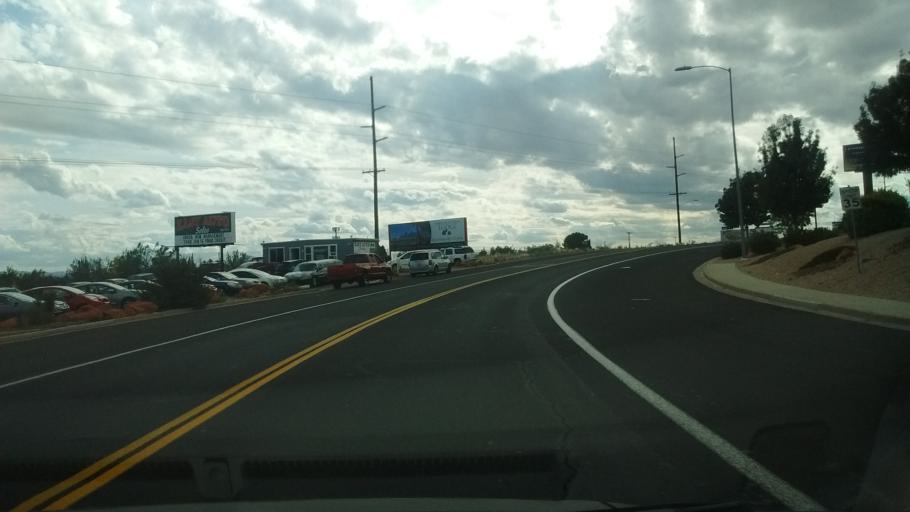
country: US
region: Utah
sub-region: Washington County
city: Washington
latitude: 37.1345
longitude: -113.5184
